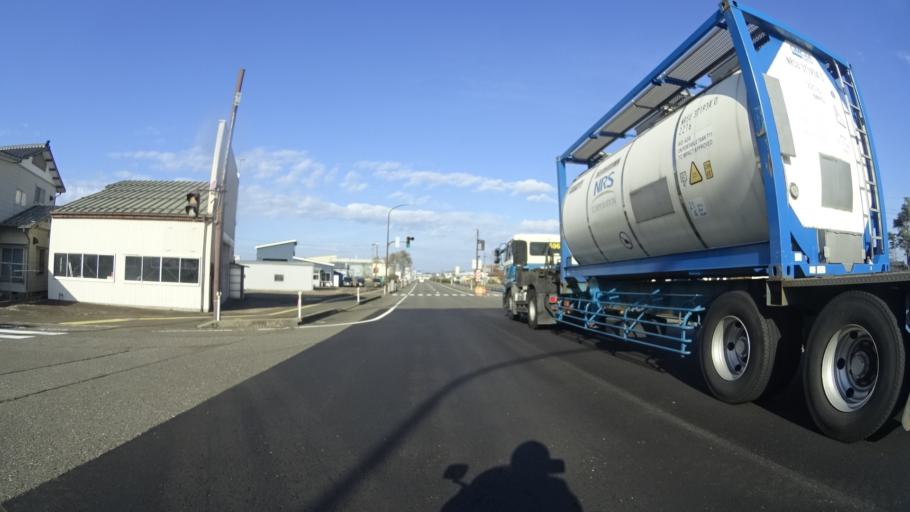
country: JP
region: Niigata
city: Joetsu
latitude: 37.1808
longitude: 138.2698
